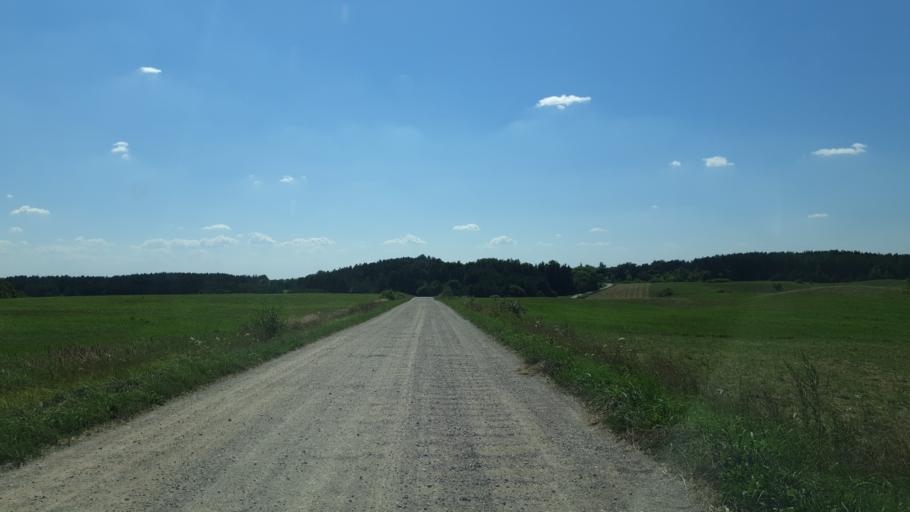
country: LT
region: Vilnius County
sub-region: Vilniaus Rajonas
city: Vievis
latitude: 54.8952
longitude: 24.8651
